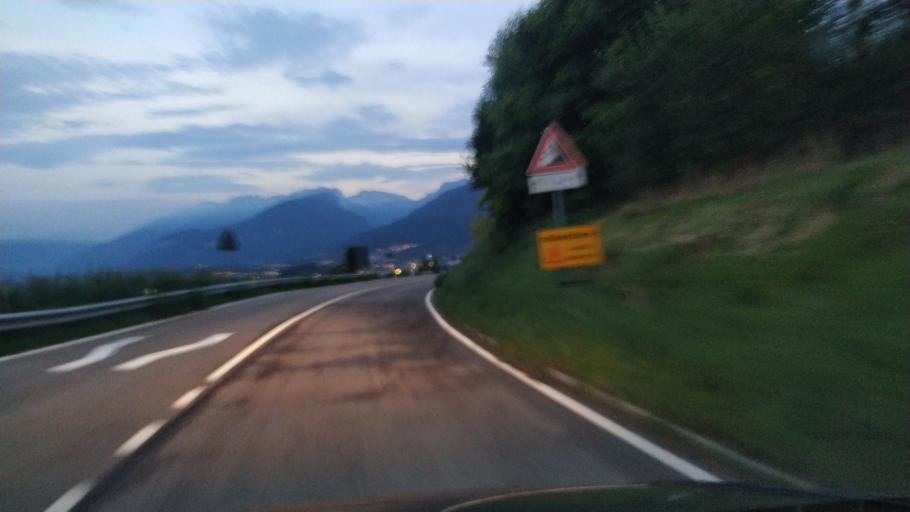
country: IT
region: Trentino-Alto Adige
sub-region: Provincia di Trento
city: Revo
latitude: 46.3921
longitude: 11.0534
